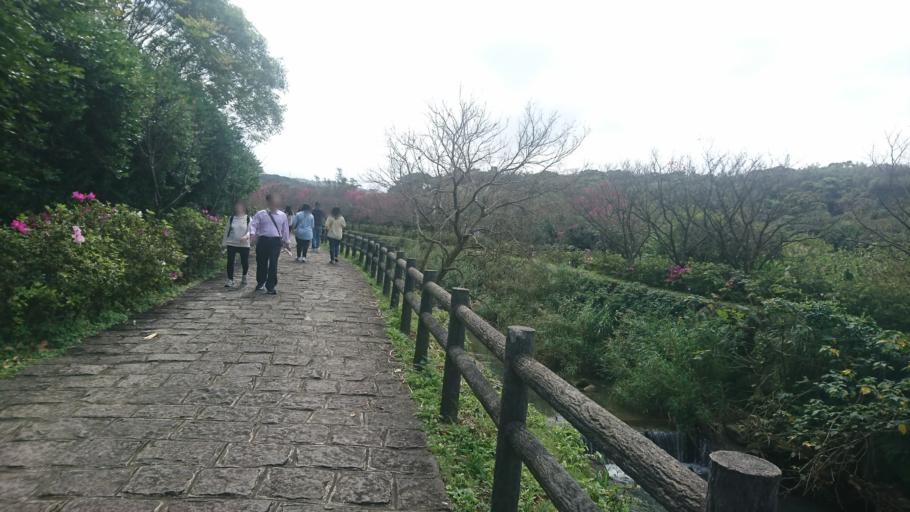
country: TW
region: Taipei
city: Taipei
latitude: 25.2670
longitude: 121.5121
